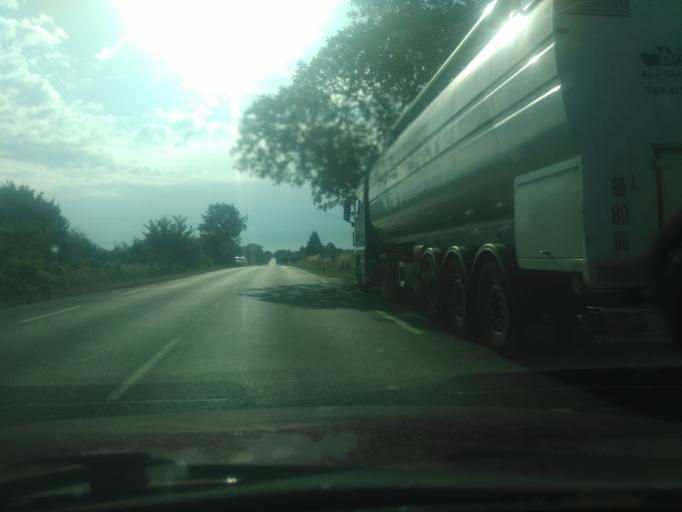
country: FR
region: Pays de la Loire
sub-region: Departement de la Vendee
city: Bazoges-en-Pareds
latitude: 46.6800
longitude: -0.9590
